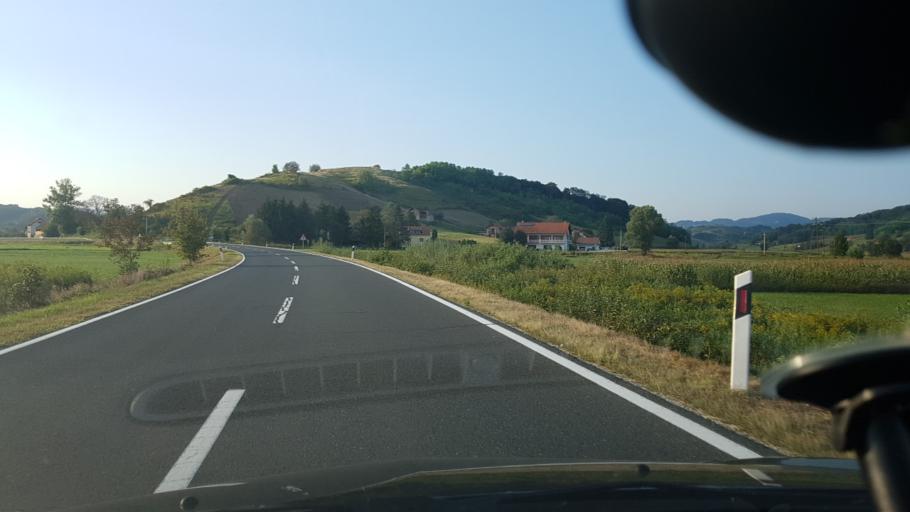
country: HR
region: Krapinsko-Zagorska
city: Pregrada
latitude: 46.1111
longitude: 15.8126
